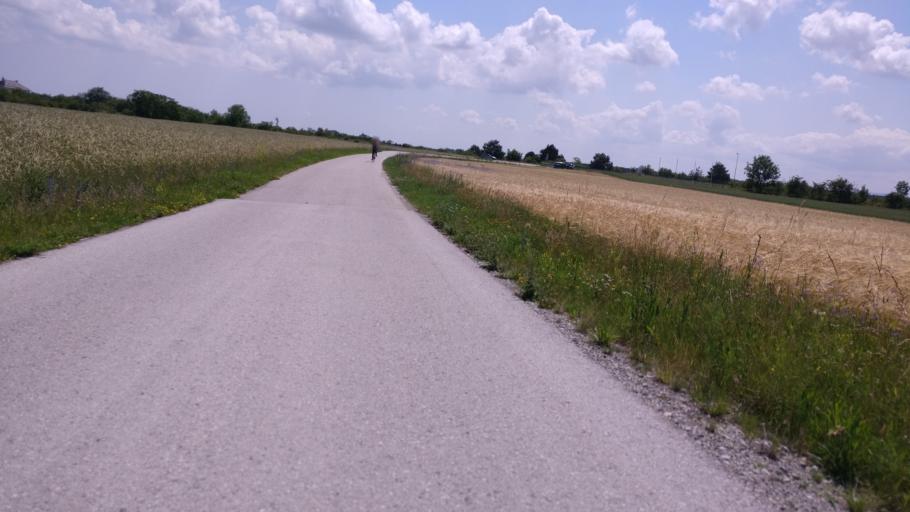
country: AT
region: Lower Austria
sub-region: Politischer Bezirk Wiener Neustadt
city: Sollenau
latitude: 47.9019
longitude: 16.2676
